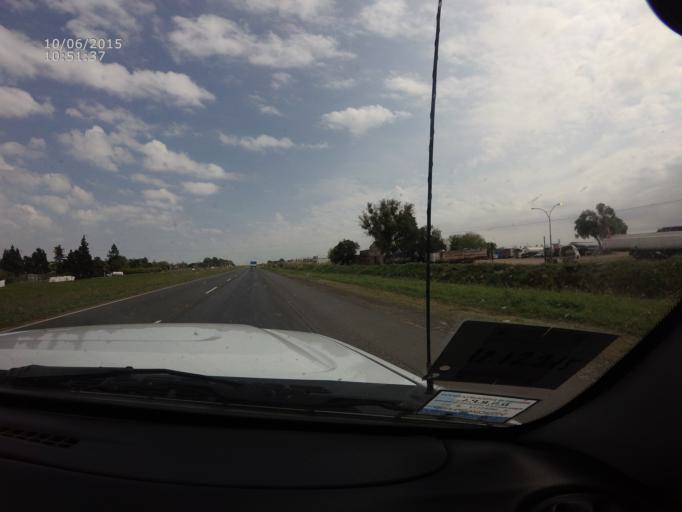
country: AR
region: Buenos Aires
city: San Nicolas de los Arroyos
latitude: -33.3613
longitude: -60.2586
